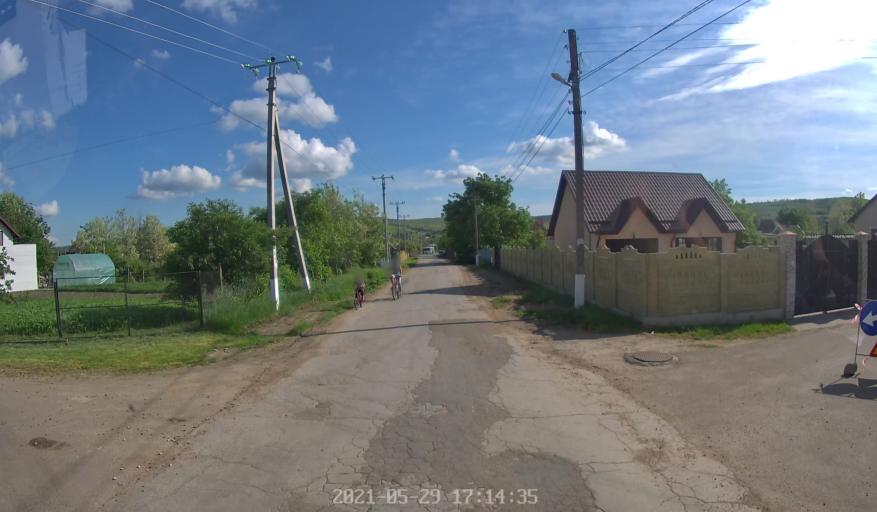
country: MD
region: Laloveni
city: Ialoveni
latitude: 46.8351
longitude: 28.8482
